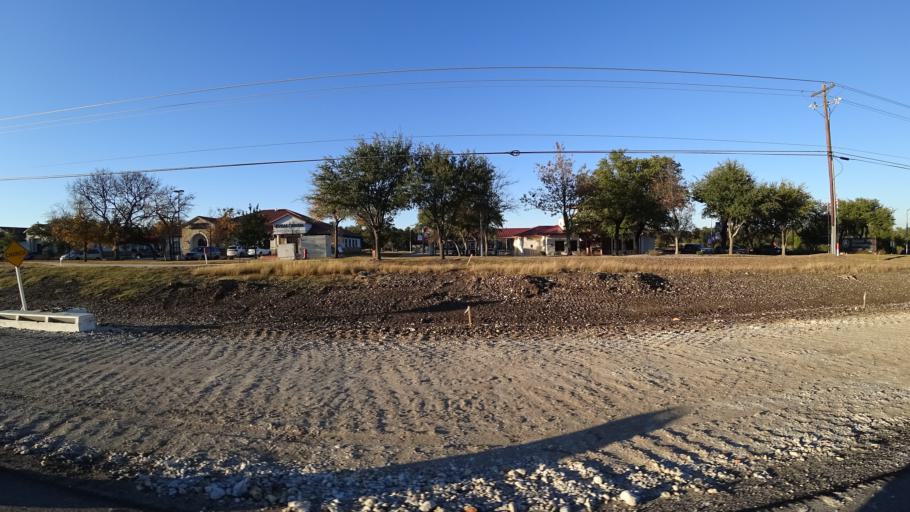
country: US
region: Texas
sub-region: Williamson County
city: Cedar Park
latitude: 30.5294
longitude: -97.8015
